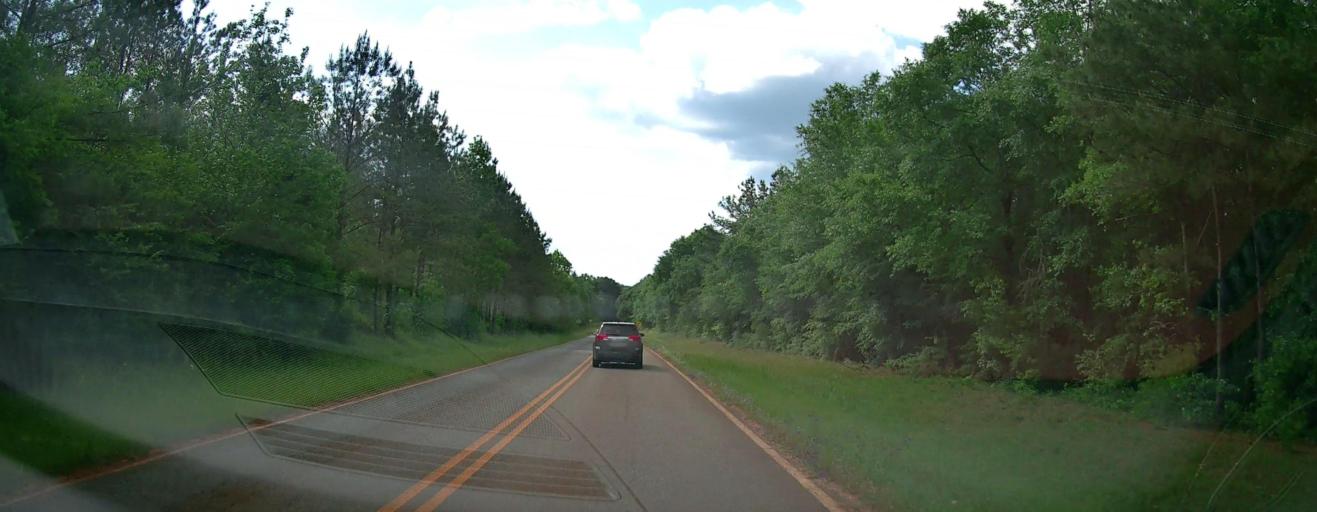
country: US
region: Georgia
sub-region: Laurens County
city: East Dublin
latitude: 32.7374
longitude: -82.9153
